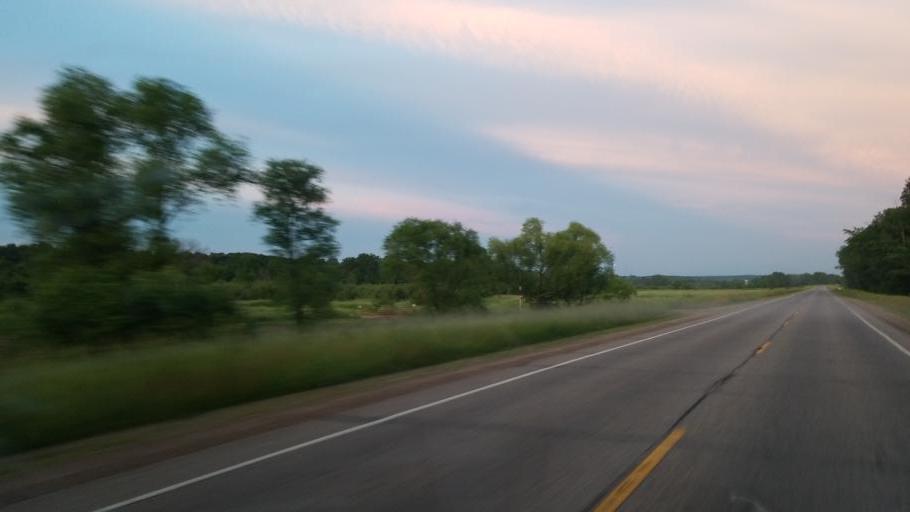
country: US
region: Wisconsin
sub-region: Juneau County
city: Elroy
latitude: 43.7599
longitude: -90.3038
